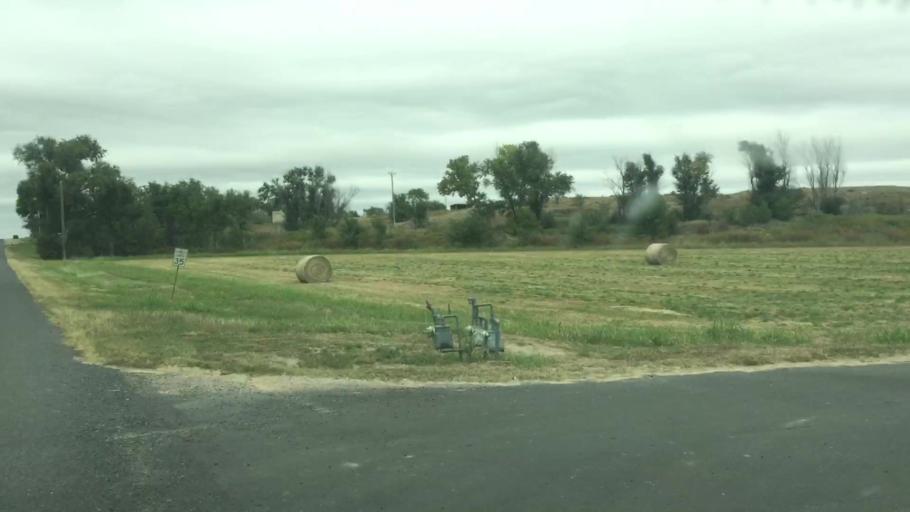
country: US
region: Kansas
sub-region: Hamilton County
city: Syracuse
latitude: 38.0574
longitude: -102.1186
